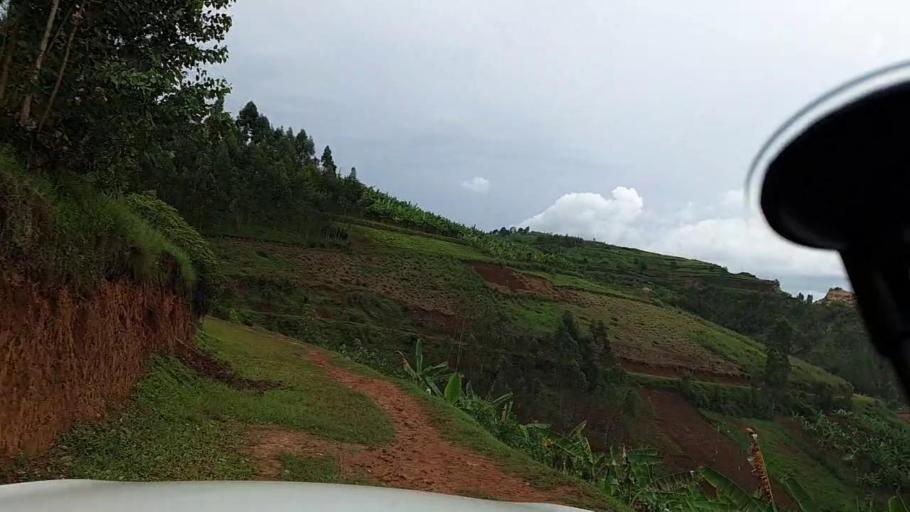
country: RW
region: Southern Province
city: Gitarama
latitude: -2.0791
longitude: 29.6436
